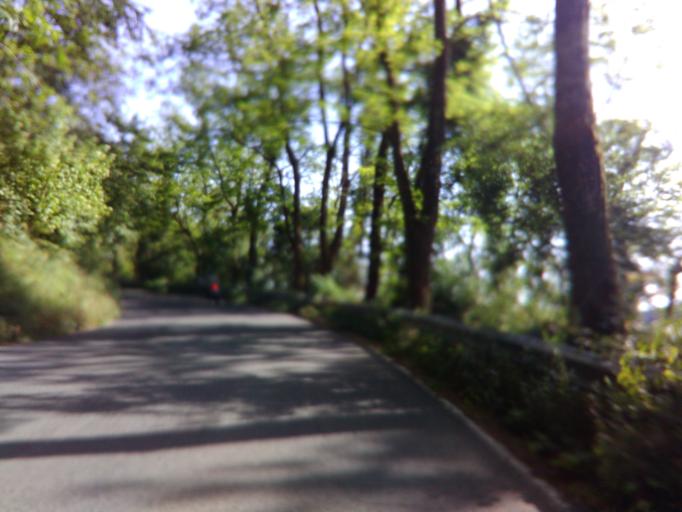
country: IT
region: Tuscany
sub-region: Provincia di Massa-Carrara
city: Fosdinovo
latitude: 44.1191
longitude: 10.0649
